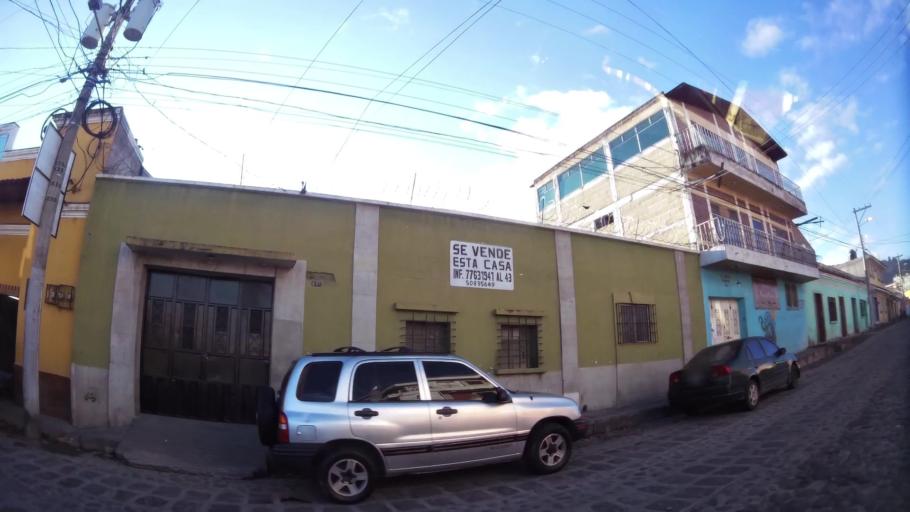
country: GT
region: Quetzaltenango
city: Quetzaltenango
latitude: 14.8340
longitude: -91.5243
